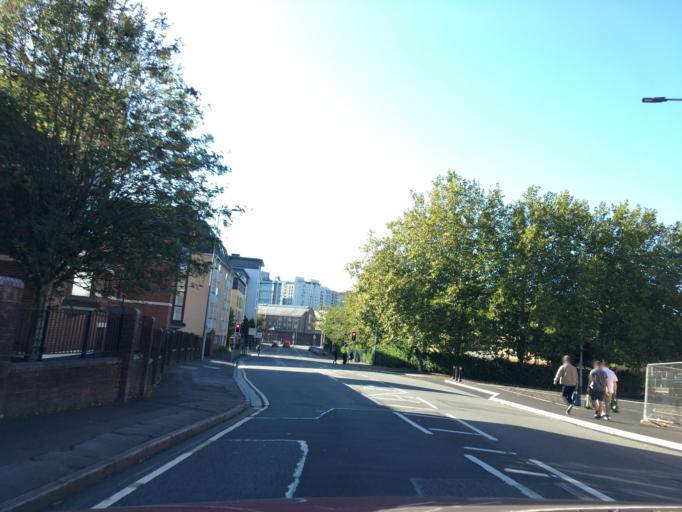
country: GB
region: Wales
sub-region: Cardiff
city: Cardiff
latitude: 51.4806
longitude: -3.1631
